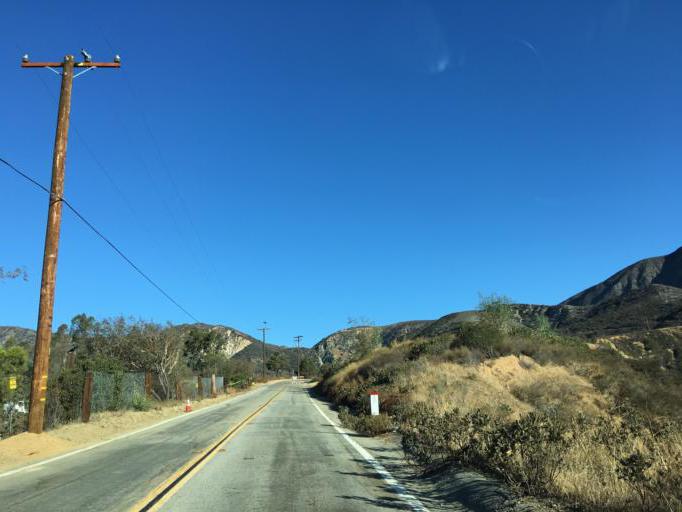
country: US
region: California
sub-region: Los Angeles County
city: San Fernando
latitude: 34.3315
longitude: -118.3416
